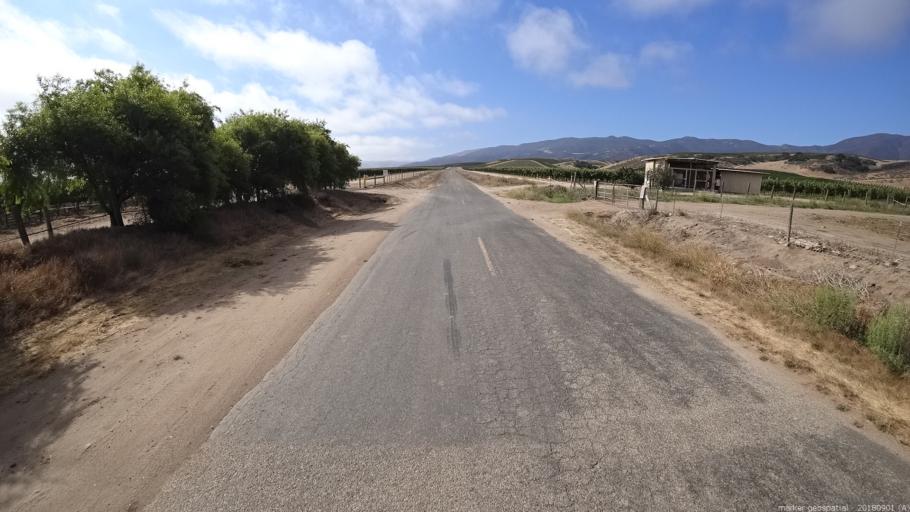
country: US
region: California
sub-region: Monterey County
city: Soledad
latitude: 36.3595
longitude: -121.3355
